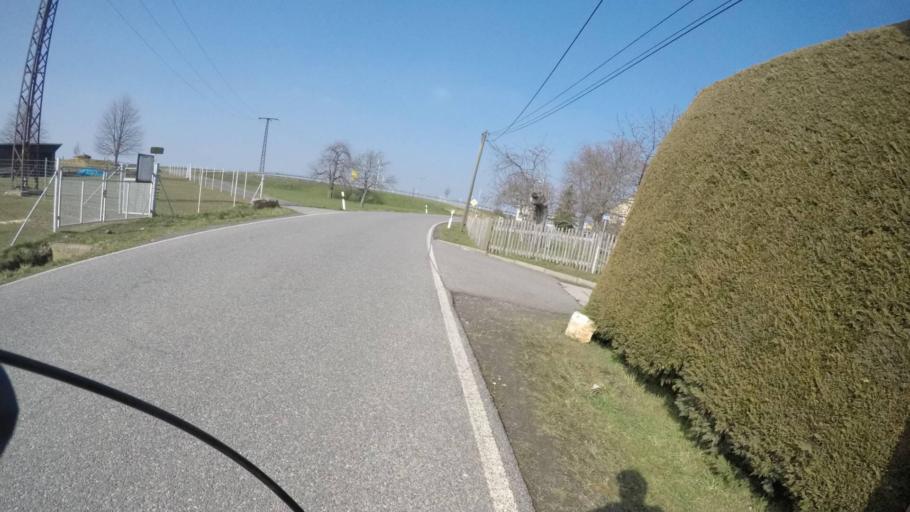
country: DE
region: Thuringia
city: Juckelberg
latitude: 50.9135
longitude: 12.6582
